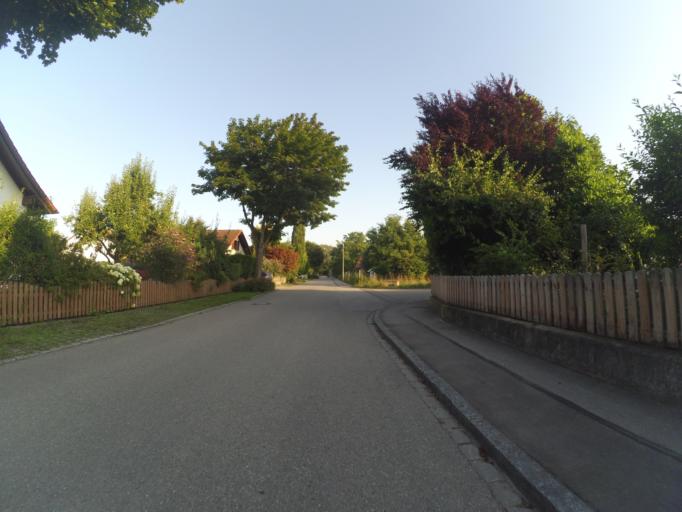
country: DE
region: Bavaria
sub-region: Swabia
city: Buchloe
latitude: 48.0192
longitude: 10.7193
